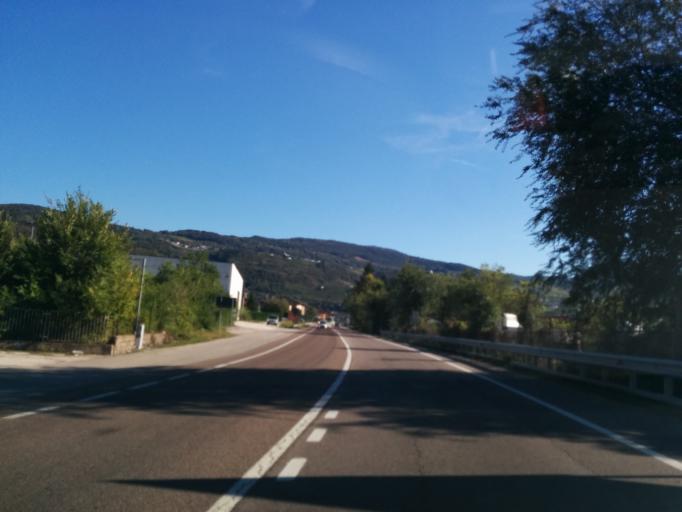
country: IT
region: Trentino-Alto Adige
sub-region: Provincia di Trento
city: Lavis
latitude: 46.1435
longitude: 11.1009
